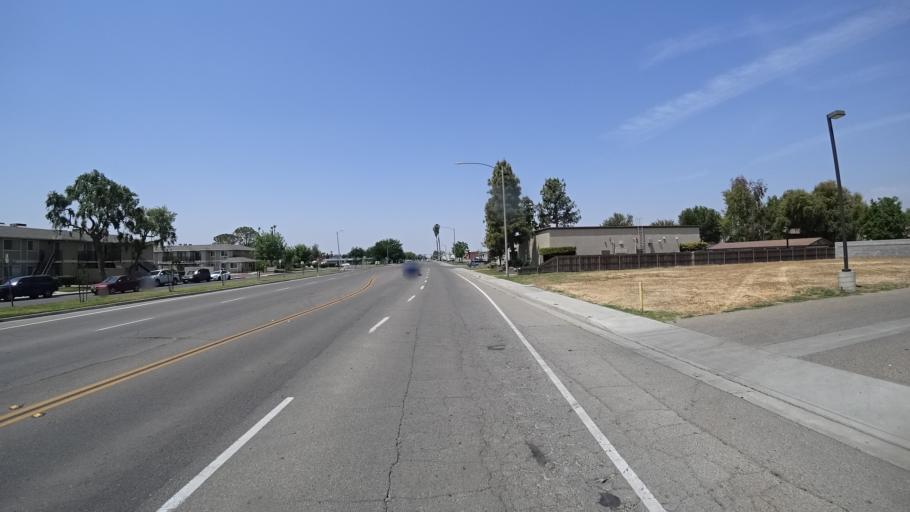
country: US
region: California
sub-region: Kings County
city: Lemoore
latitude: 36.3135
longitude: -119.7765
